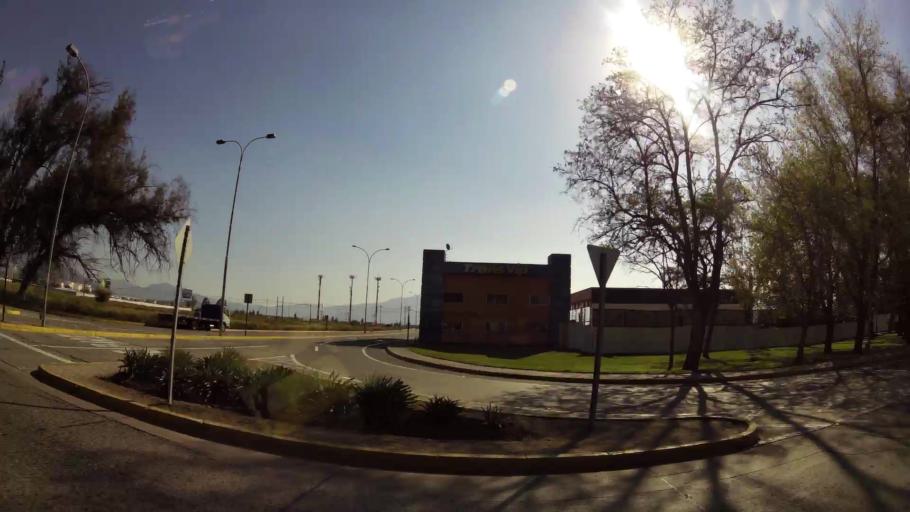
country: CL
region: Santiago Metropolitan
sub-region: Provincia de Santiago
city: Lo Prado
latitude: -33.4054
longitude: -70.7918
